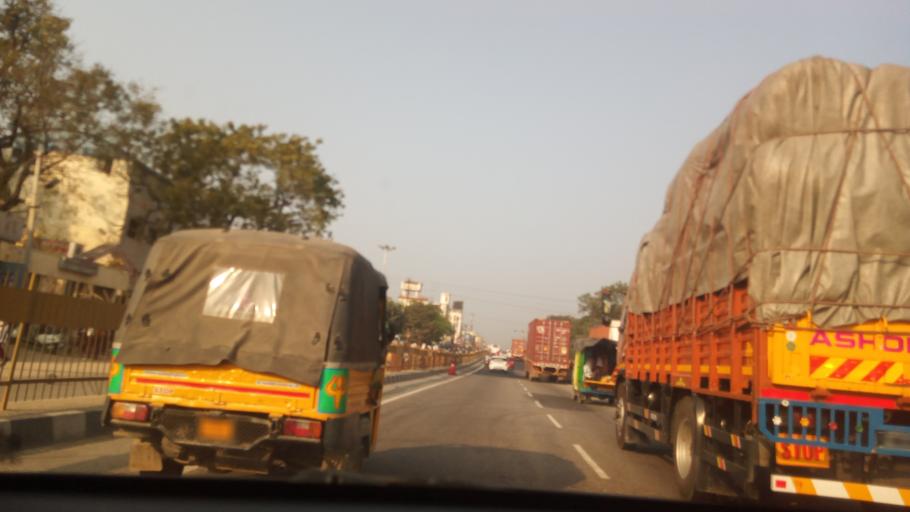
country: IN
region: Tamil Nadu
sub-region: Vellore
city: Ambur
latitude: 12.7805
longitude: 78.7175
